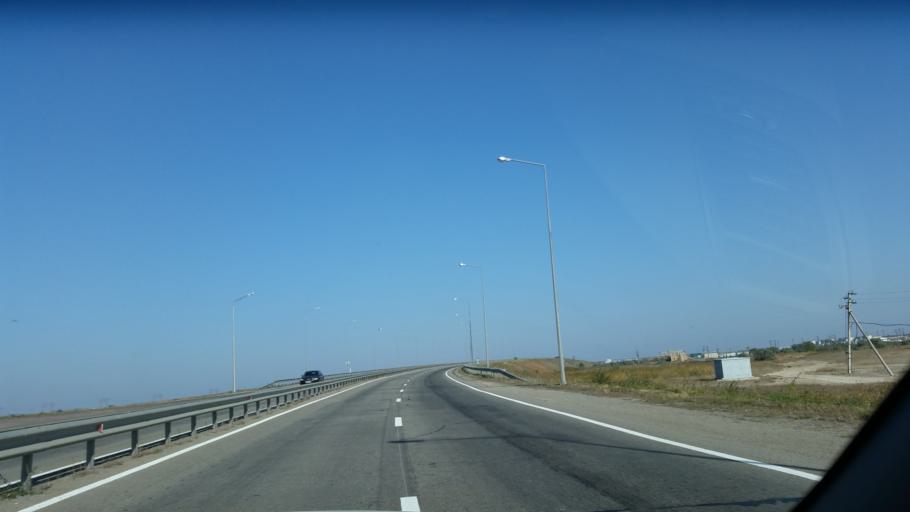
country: KZ
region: Astana Qalasy
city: Astana
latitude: 51.2497
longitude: 71.3423
